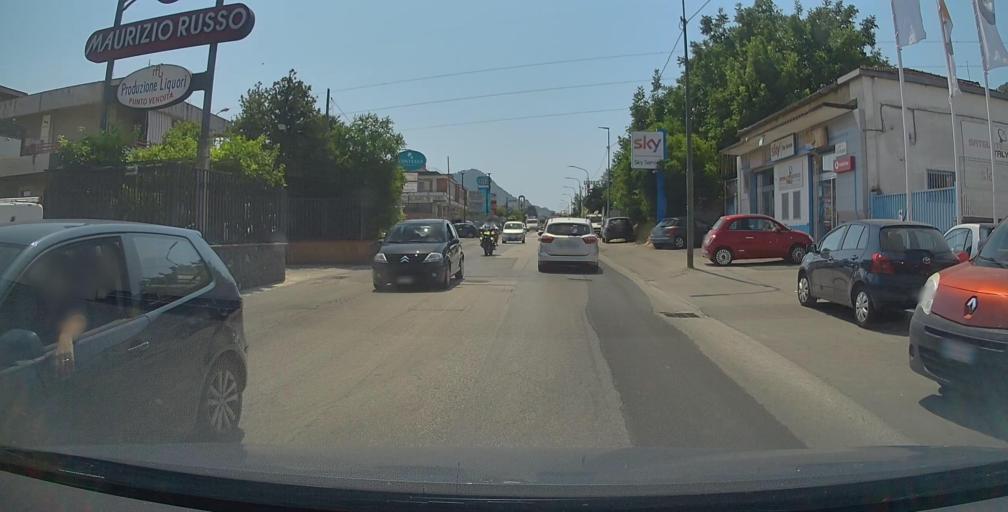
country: IT
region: Campania
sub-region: Provincia di Salerno
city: Nocera Superiore
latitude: 40.7270
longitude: 14.6915
